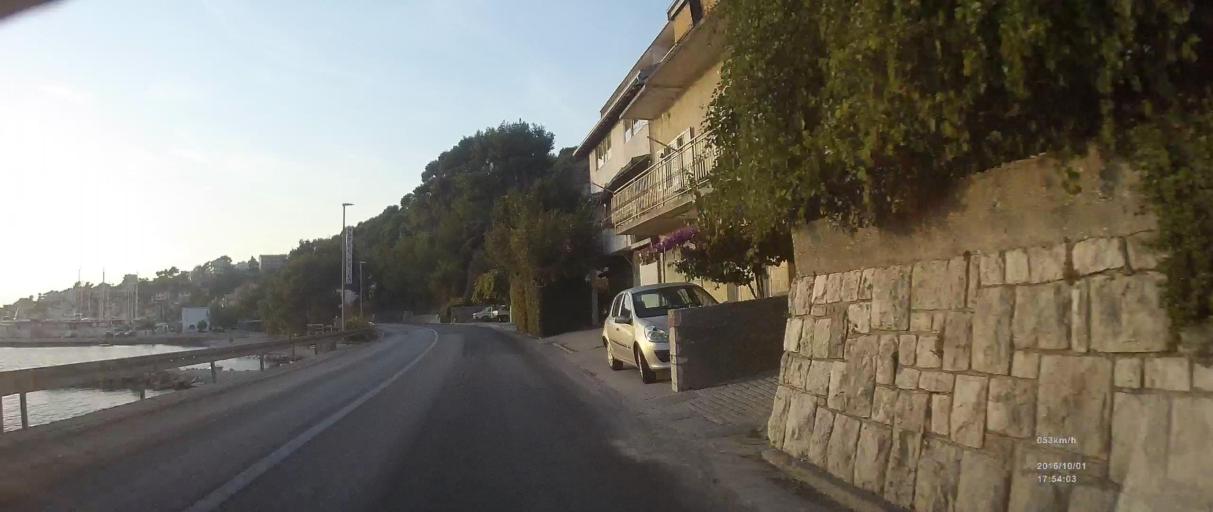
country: HR
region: Splitsko-Dalmatinska
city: Jesenice
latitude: 43.4601
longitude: 16.6038
